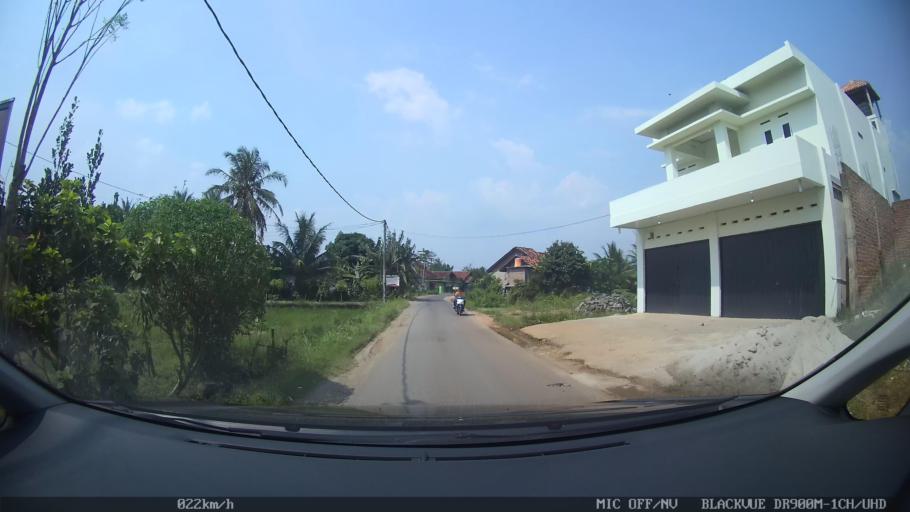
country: ID
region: Lampung
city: Natar
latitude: -5.3048
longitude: 105.2358
